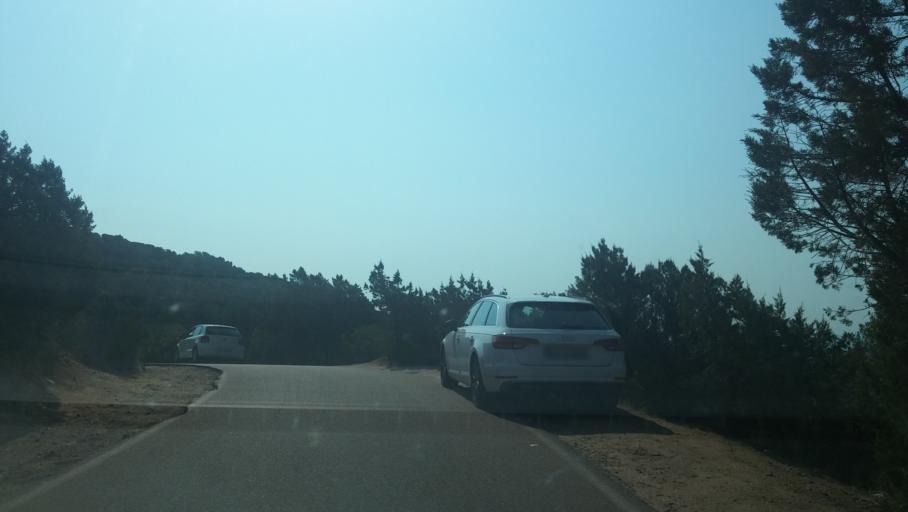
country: IT
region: Sardinia
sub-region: Provincia di Olbia-Tempio
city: La Maddalena
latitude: 41.1857
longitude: 9.4565
